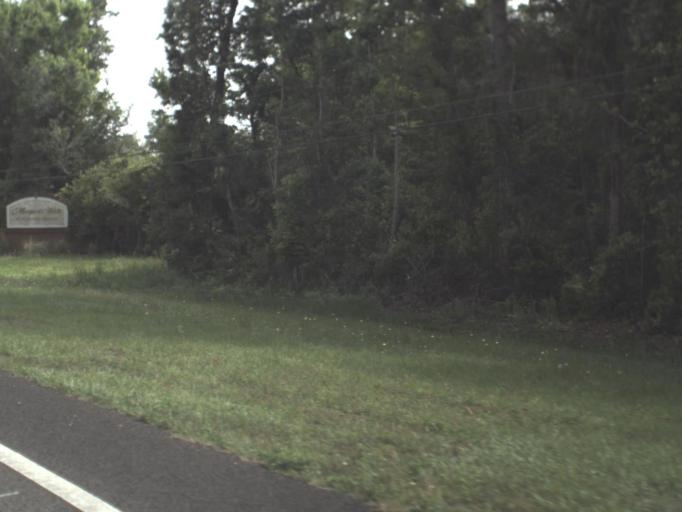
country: US
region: Florida
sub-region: Clay County
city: Green Cove Springs
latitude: 30.0470
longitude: -81.7084
